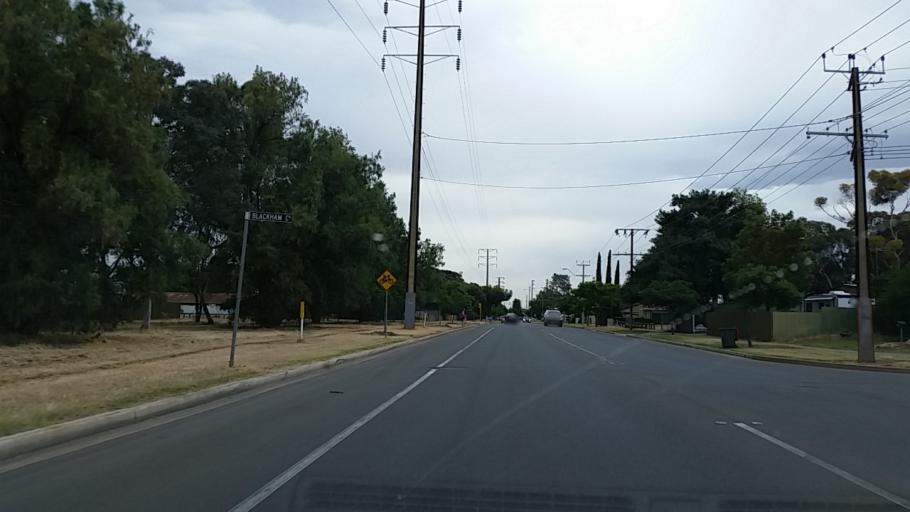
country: AU
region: South Australia
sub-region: Playford
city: Smithfield
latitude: -34.6770
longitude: 138.6831
